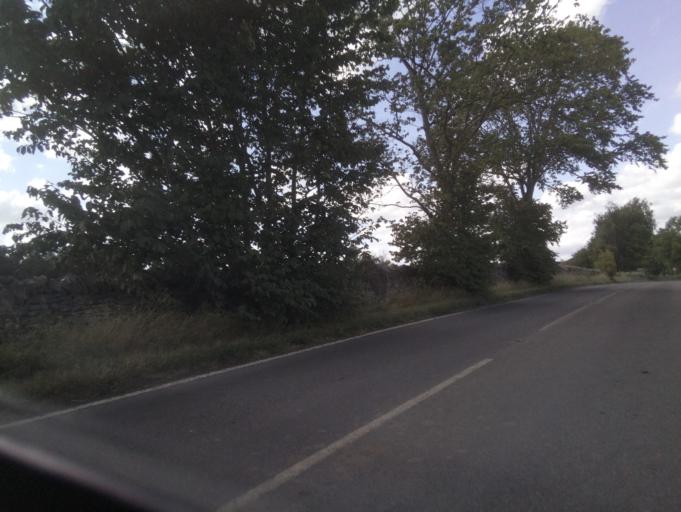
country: GB
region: England
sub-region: North Yorkshire
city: Leyburn
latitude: 54.2803
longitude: -1.7826
